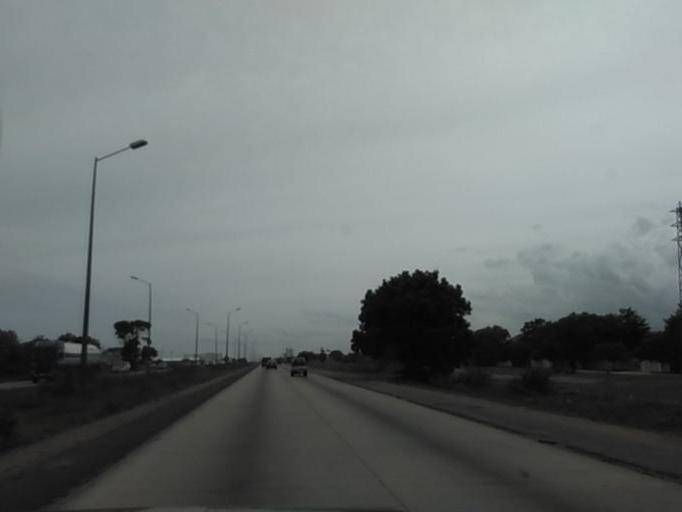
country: GH
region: Greater Accra
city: Medina Estates
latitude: 5.6433
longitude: -0.1229
